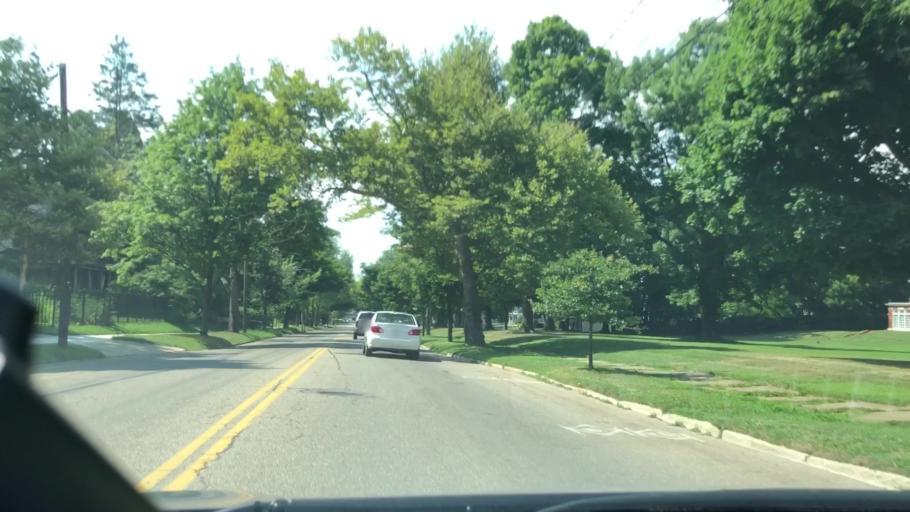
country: US
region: Ohio
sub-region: Summit County
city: Akron
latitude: 41.1004
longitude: -81.5510
